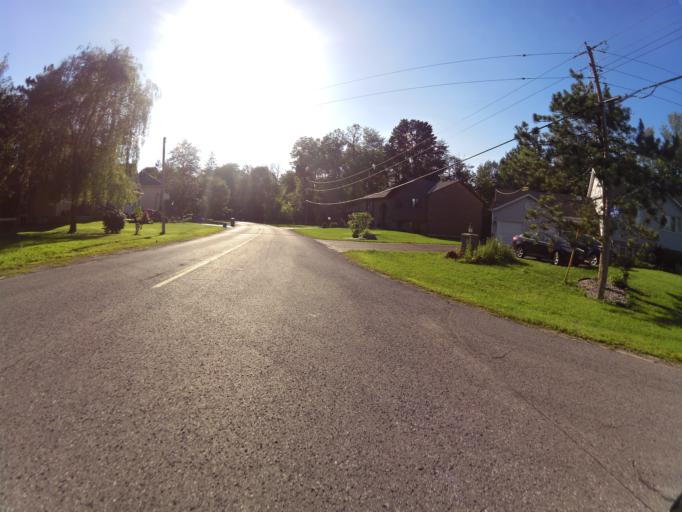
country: CA
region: Ontario
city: Bells Corners
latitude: 45.3240
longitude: -75.7398
